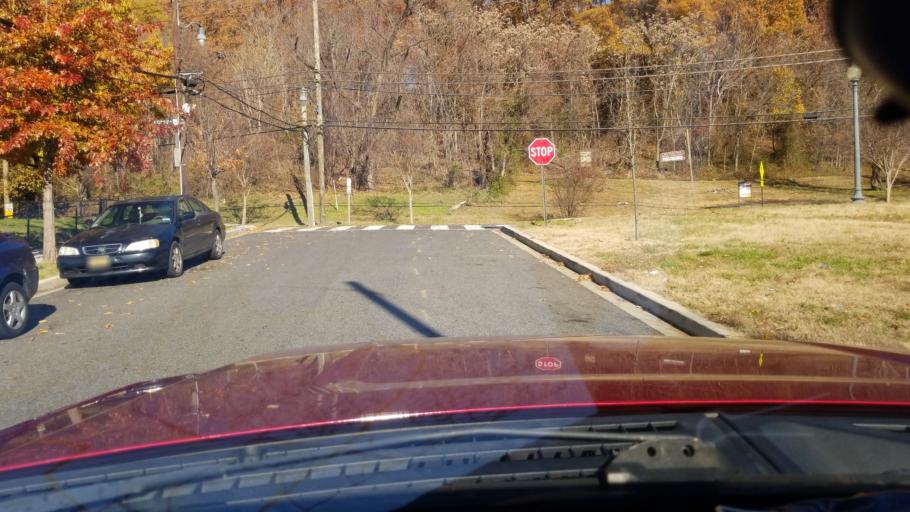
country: US
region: Maryland
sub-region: Prince George's County
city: Capitol Heights
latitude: 38.8931
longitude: -76.9445
